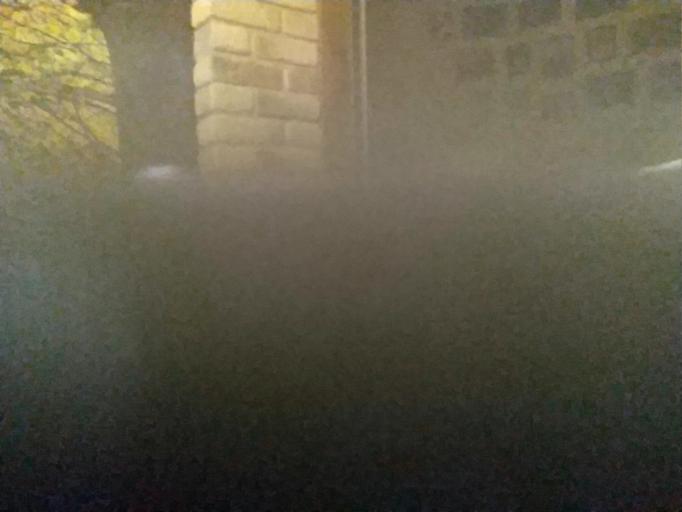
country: RU
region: Moskovskaya
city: Vysokovsk
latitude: 56.2246
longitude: 36.5462
